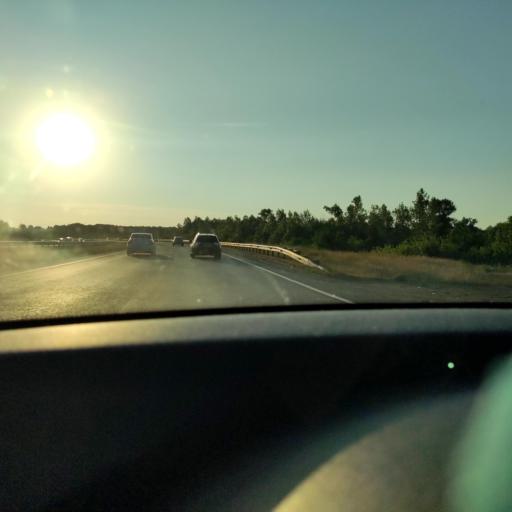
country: RU
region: Samara
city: Kinel'
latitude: 53.2586
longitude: 50.5758
